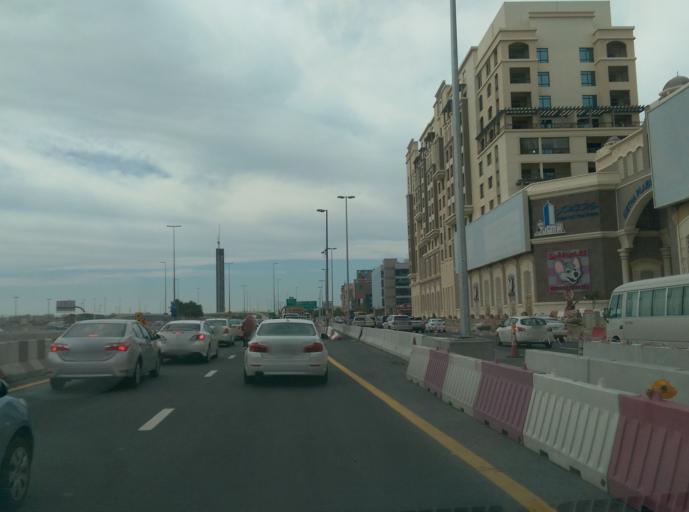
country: AE
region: Ash Shariqah
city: Sharjah
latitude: 25.2308
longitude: 55.3132
